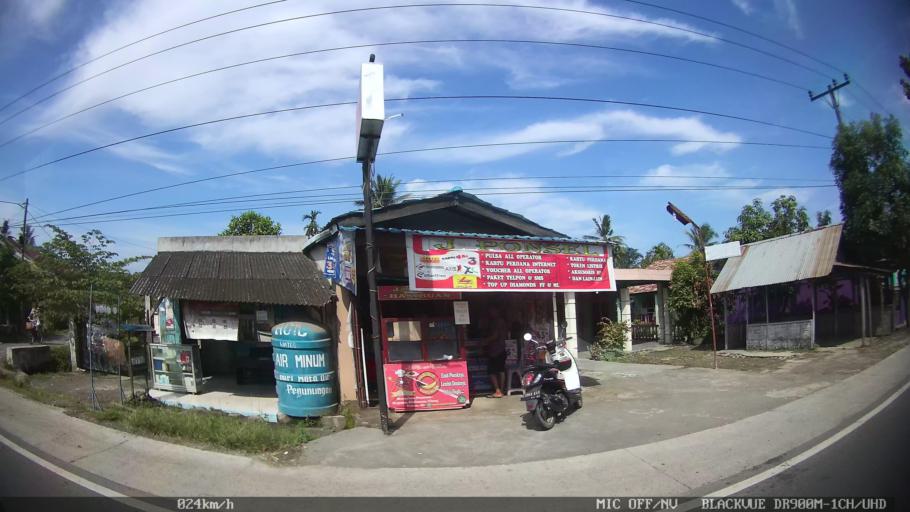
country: ID
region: North Sumatra
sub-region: Kabupaten Langkat
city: Stabat
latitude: 3.7172
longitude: 98.5036
